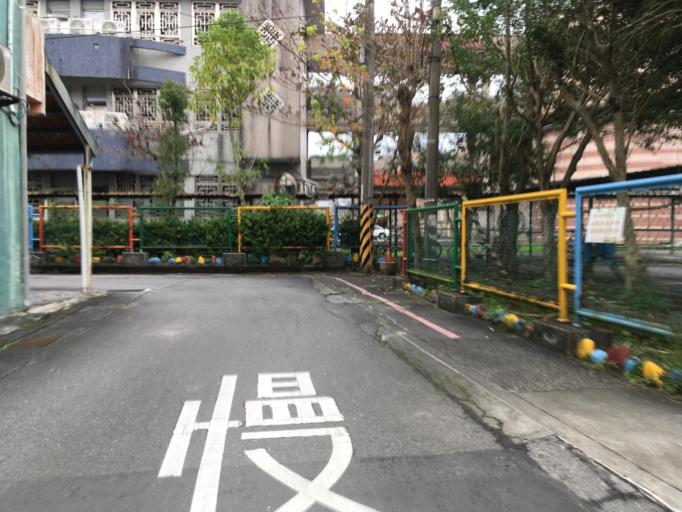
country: TW
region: Taiwan
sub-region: Yilan
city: Yilan
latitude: 24.6314
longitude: 121.7918
